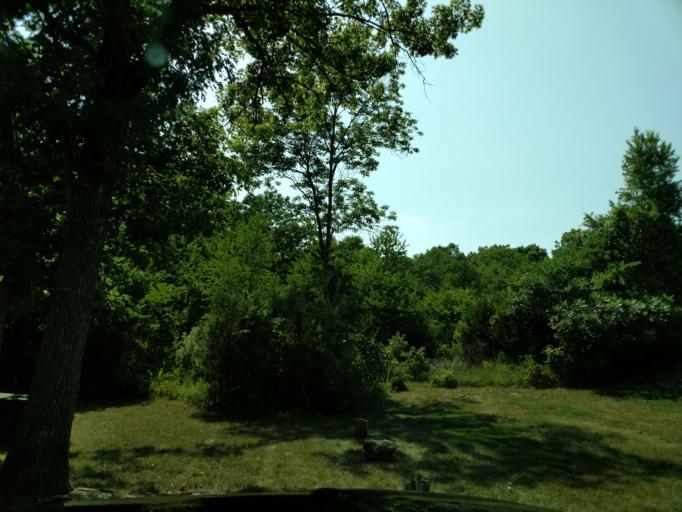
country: US
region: Missouri
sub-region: Barry County
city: Shell Knob
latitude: 36.6010
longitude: -93.5817
